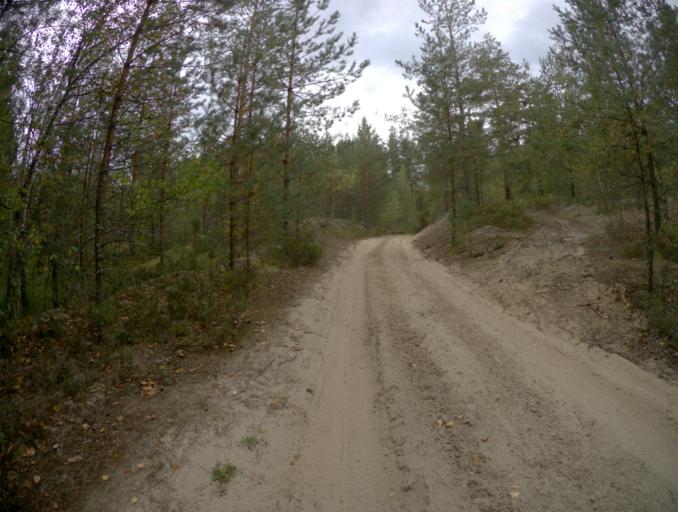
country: RU
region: Vladimir
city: Ivanishchi
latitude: 55.8354
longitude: 40.3190
